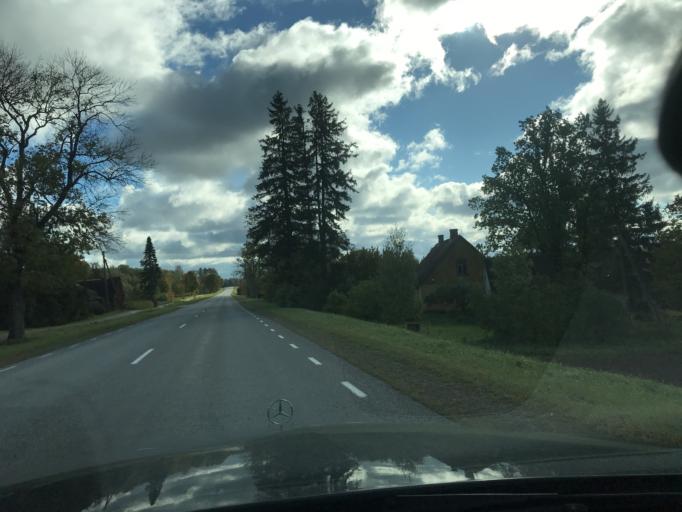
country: EE
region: Vorumaa
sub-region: Antsla vald
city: Vana-Antsla
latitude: 57.9484
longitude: 26.2919
